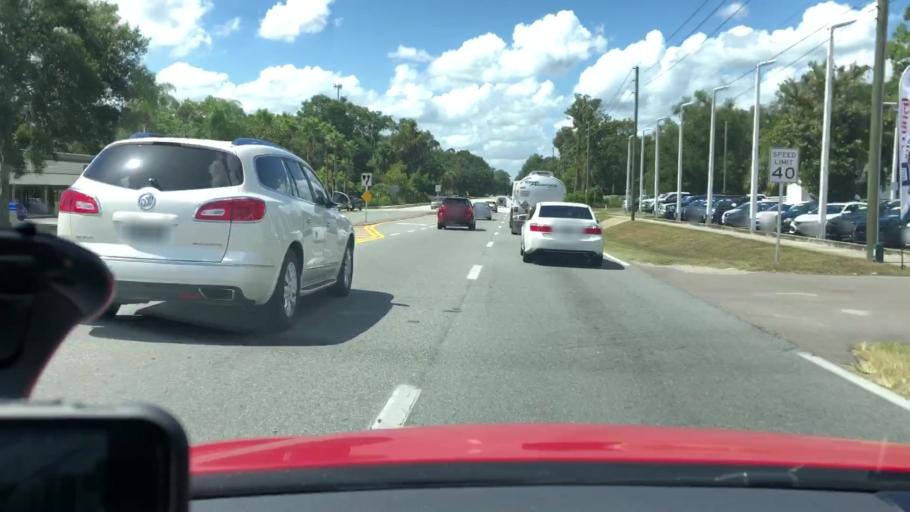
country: US
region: Florida
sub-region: Volusia County
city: De Land Southwest
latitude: 28.9989
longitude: -81.3037
